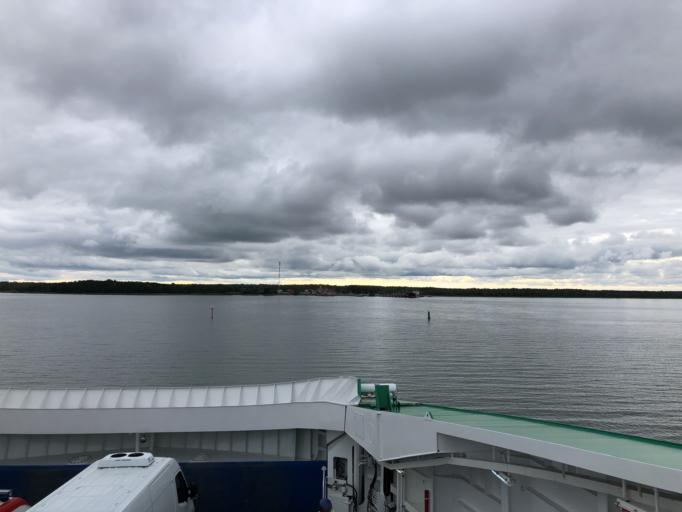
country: EE
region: Laeaene
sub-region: Vormsi vald
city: Hullo
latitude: 58.8680
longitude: 23.0647
